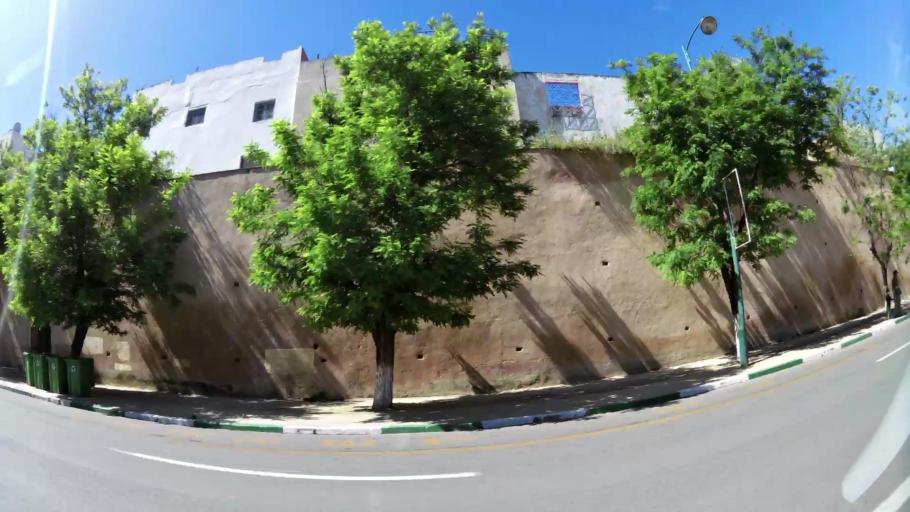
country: MA
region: Meknes-Tafilalet
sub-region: Meknes
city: Meknes
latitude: 33.8836
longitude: -5.5466
